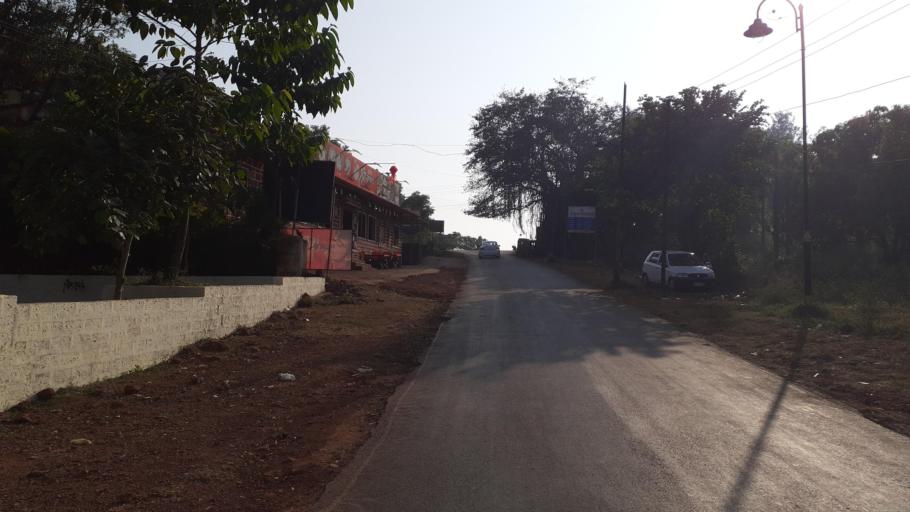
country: IN
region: Maharashtra
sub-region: Ratnagiri
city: Ratnagiri
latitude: 17.1447
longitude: 73.2697
